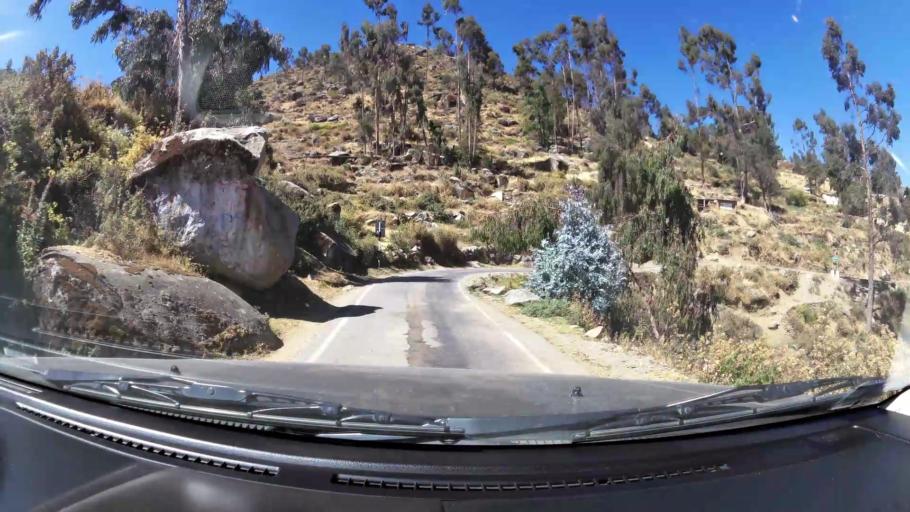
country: PE
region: Huancavelica
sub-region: Huaytara
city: Quito-Arma
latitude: -13.6835
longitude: -75.3747
